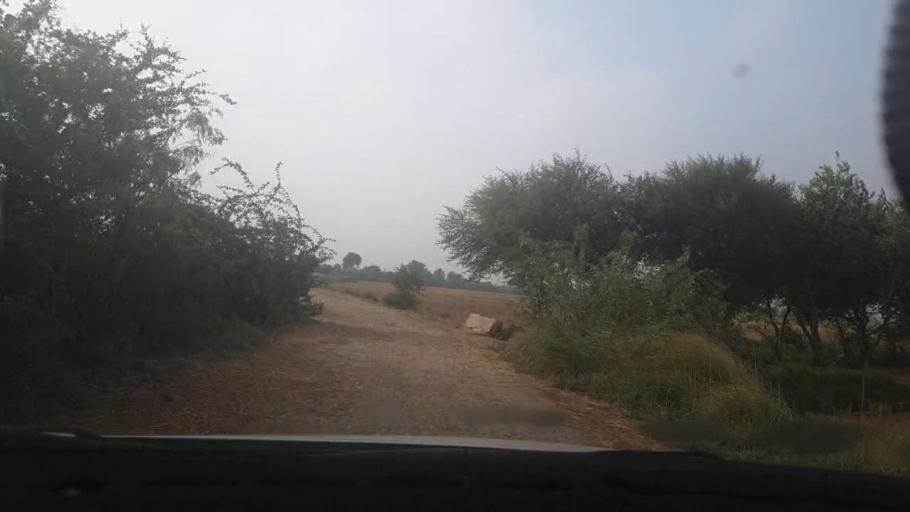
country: PK
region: Sindh
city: Tando Muhammad Khan
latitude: 25.0819
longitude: 68.5131
